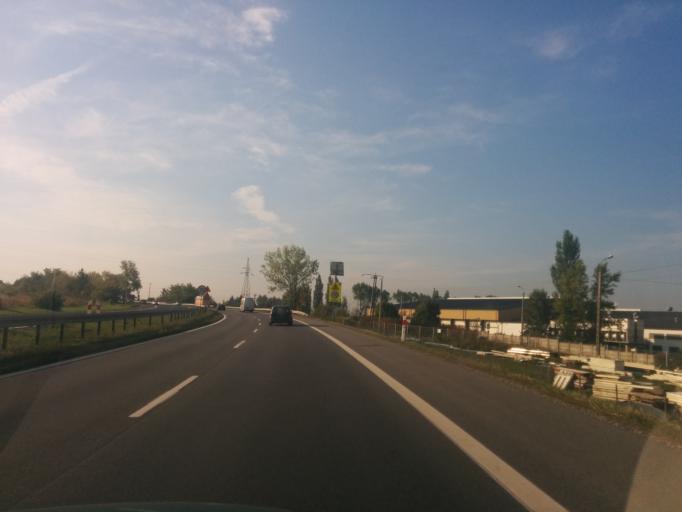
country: PL
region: Masovian Voivodeship
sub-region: Powiat piaseczynski
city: Tarczyn
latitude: 51.9733
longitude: 20.8349
